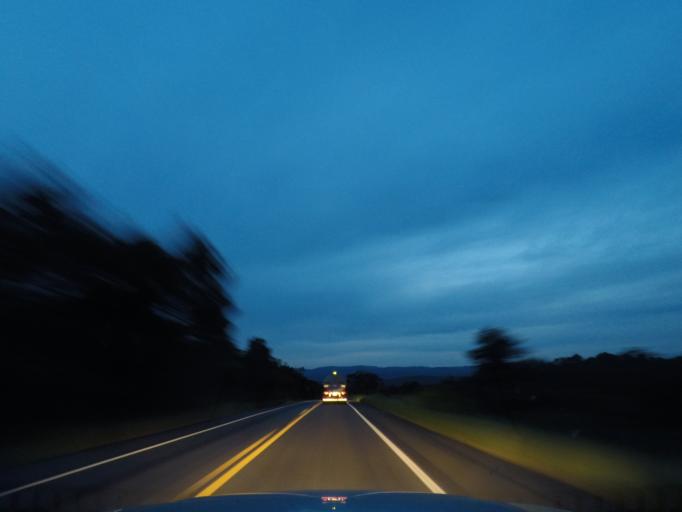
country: BR
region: Bahia
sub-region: Andarai
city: Vera Cruz
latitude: -12.4952
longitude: -41.3144
